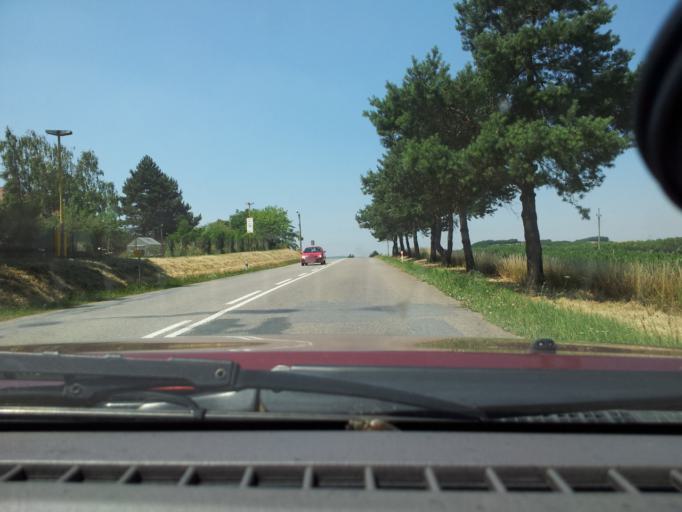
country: CZ
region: South Moravian
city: Mutenice
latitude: 48.9089
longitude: 17.0145
